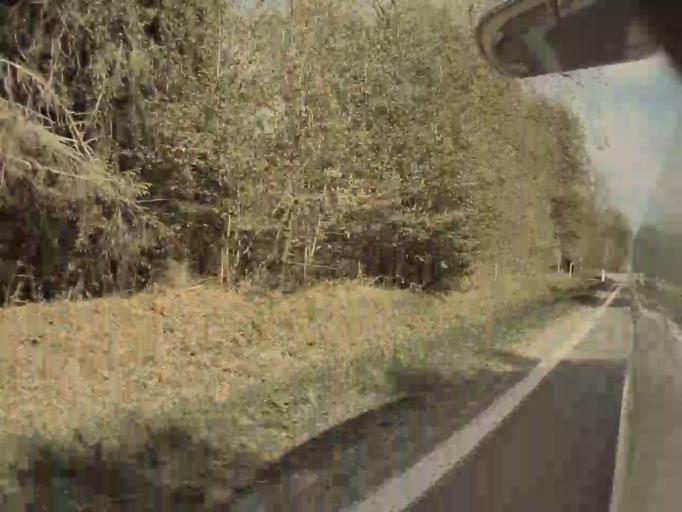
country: BE
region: Wallonia
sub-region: Province du Luxembourg
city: Tellin
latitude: 50.0478
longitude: 5.2097
